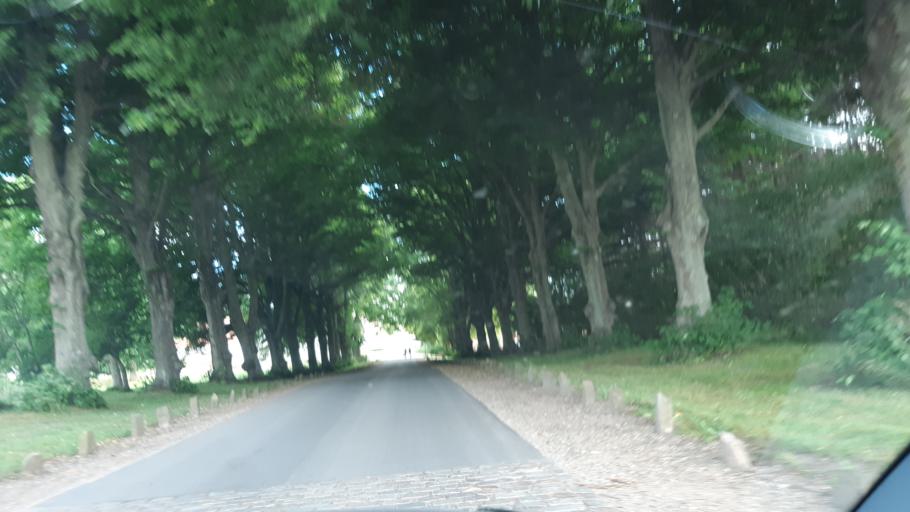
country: DK
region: Zealand
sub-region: Odsherred Kommune
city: Horve
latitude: 55.7737
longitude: 11.3905
